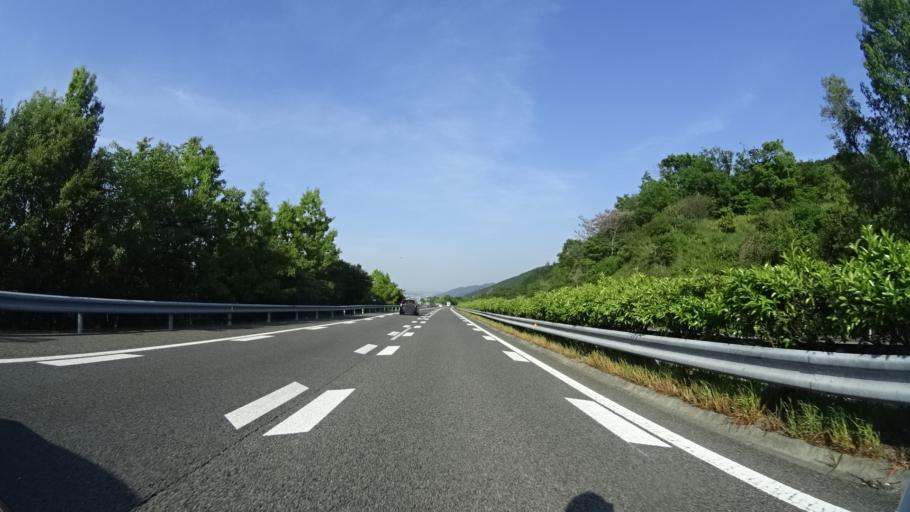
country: JP
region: Ehime
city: Saijo
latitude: 33.8841
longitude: 133.1316
